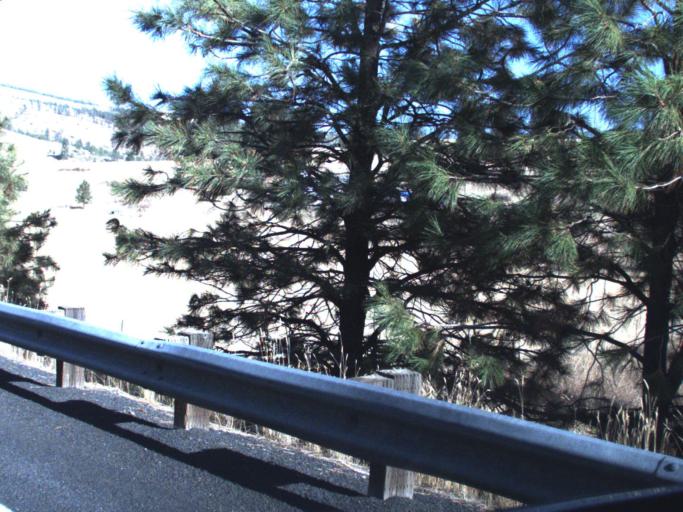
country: US
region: Washington
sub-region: Lincoln County
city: Davenport
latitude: 47.8808
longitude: -118.2651
